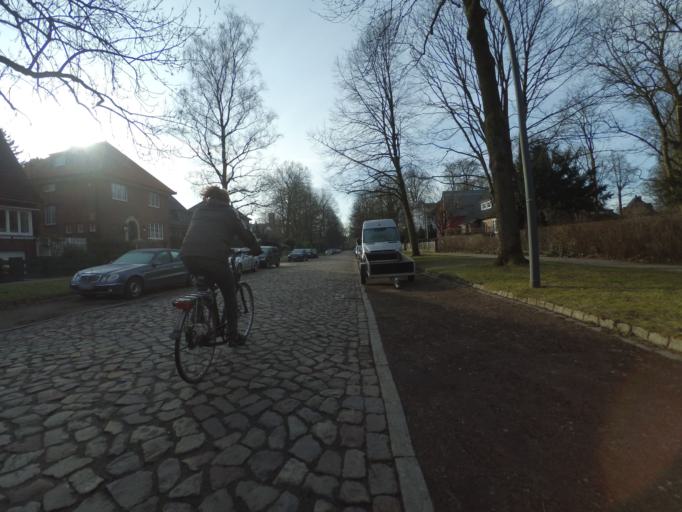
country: DE
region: Hamburg
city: Hamburg-Nord
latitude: 53.6095
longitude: 9.9734
